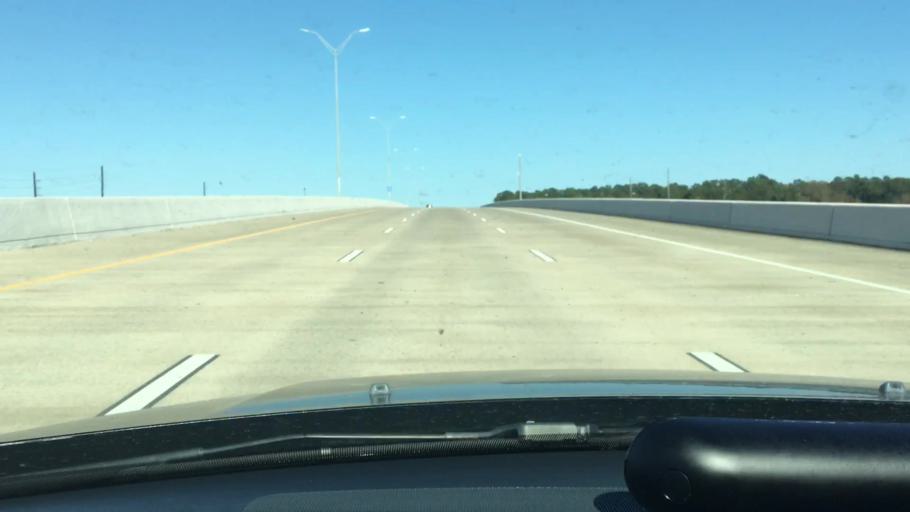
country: US
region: Texas
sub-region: Harris County
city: Sheldon
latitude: 29.8514
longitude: -95.1869
